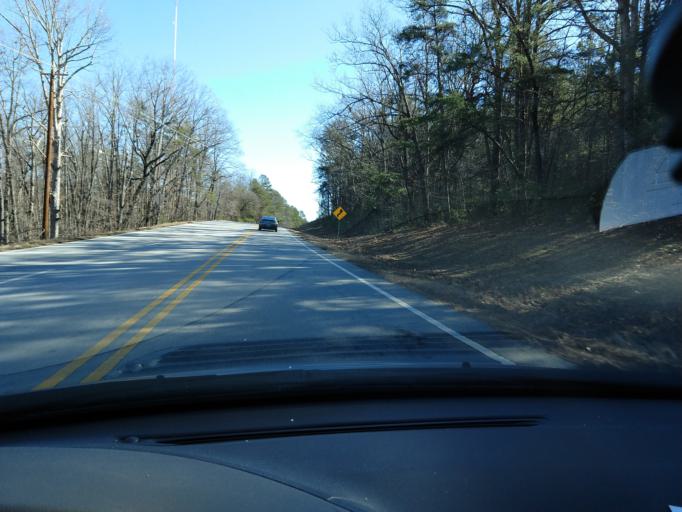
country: US
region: Georgia
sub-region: Stephens County
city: Toccoa
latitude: 34.6097
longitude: -83.3734
